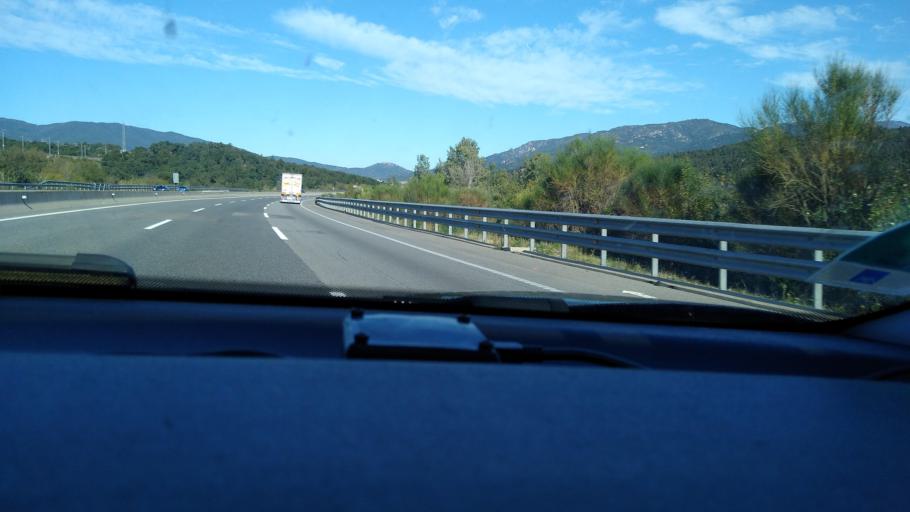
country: ES
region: Catalonia
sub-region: Provincia de Girona
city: Capmany
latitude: 42.3751
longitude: 2.8875
